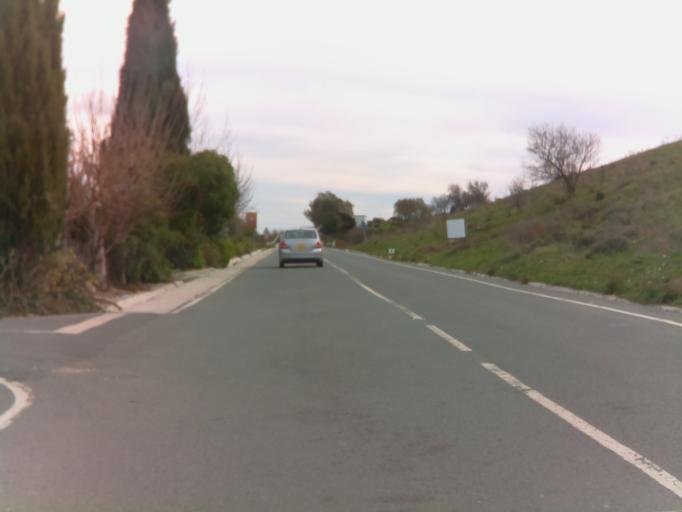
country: CY
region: Pafos
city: Polis
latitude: 34.9651
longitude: 32.4127
